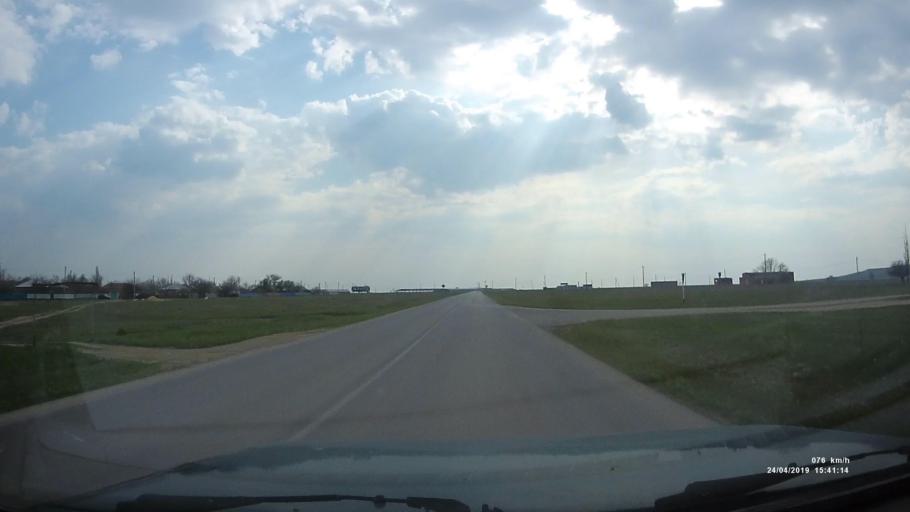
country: RU
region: Kalmykiya
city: Yashalta
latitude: 46.5737
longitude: 42.8006
